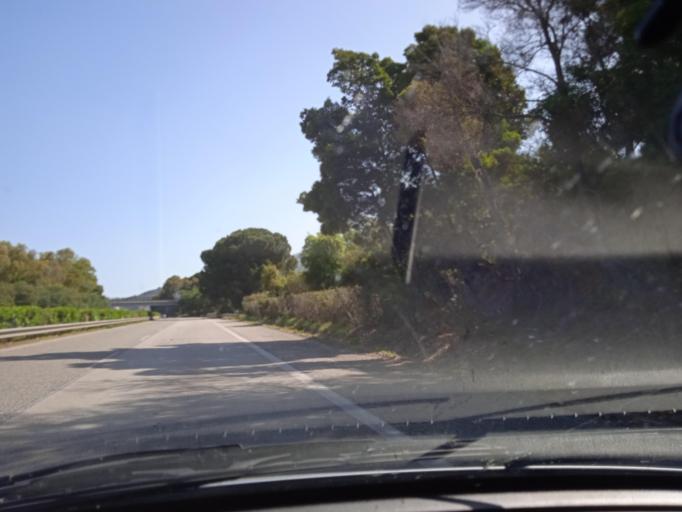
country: IT
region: Sicily
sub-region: Messina
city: Capo d'Orlando
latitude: 38.1237
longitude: 14.7290
